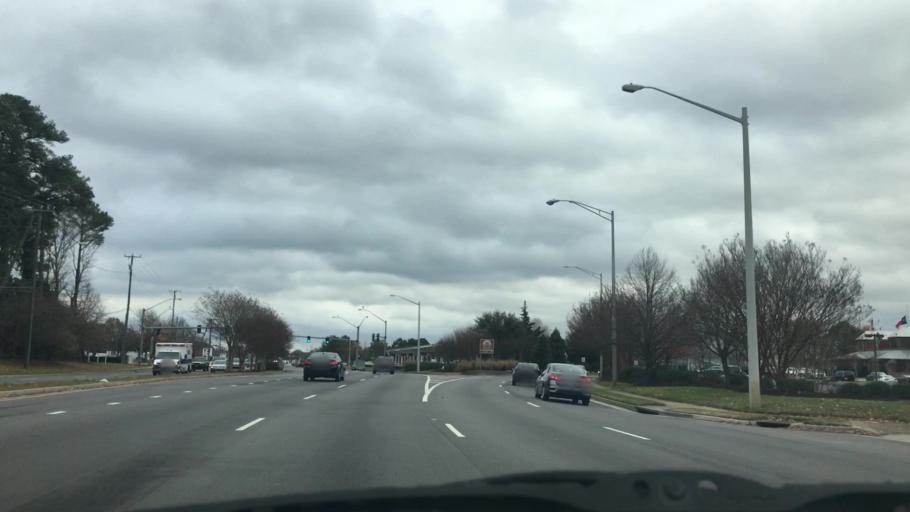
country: US
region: Virginia
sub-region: City of Chesapeake
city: Chesapeake
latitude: 36.8243
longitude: -76.1281
